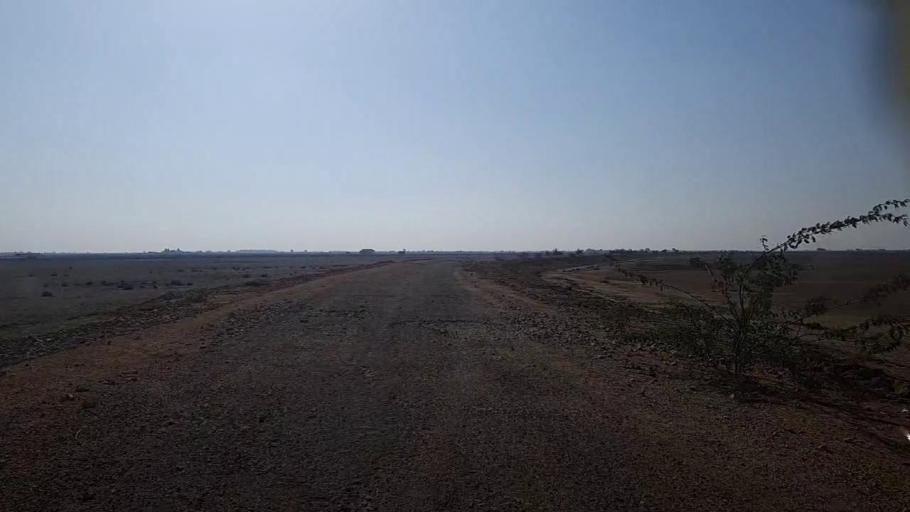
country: PK
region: Sindh
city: Mirpur Sakro
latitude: 24.5149
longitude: 67.5044
